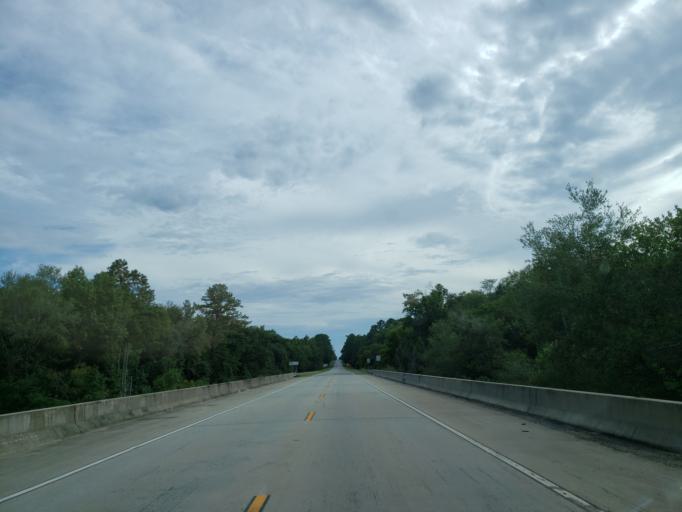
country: US
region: Georgia
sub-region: Tift County
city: Tifton
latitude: 31.5331
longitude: -83.3986
